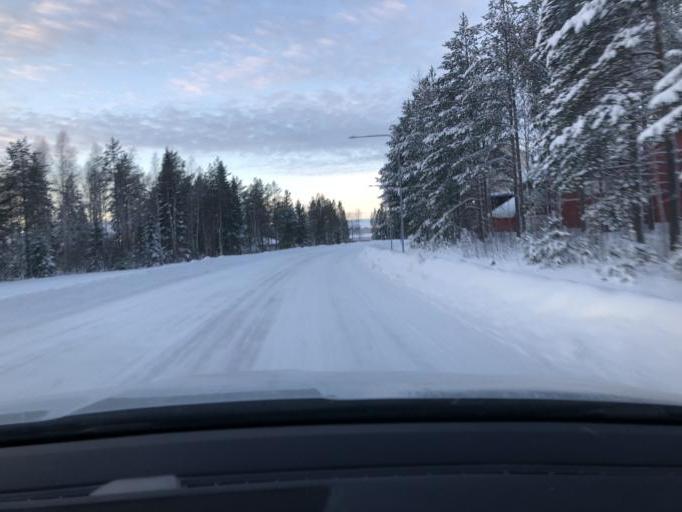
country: SE
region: Norrbotten
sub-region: Lulea Kommun
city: Bergnaset
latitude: 65.6184
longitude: 22.1207
